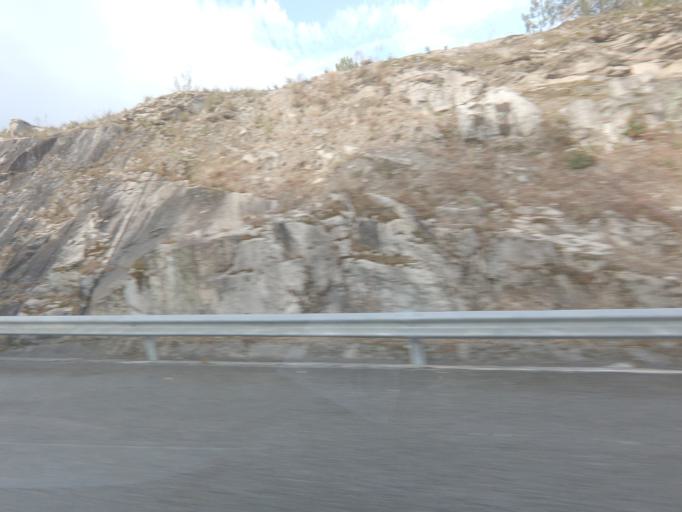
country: PT
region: Viseu
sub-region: Castro Daire
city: Castro Daire
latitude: 40.8292
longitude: -7.9364
